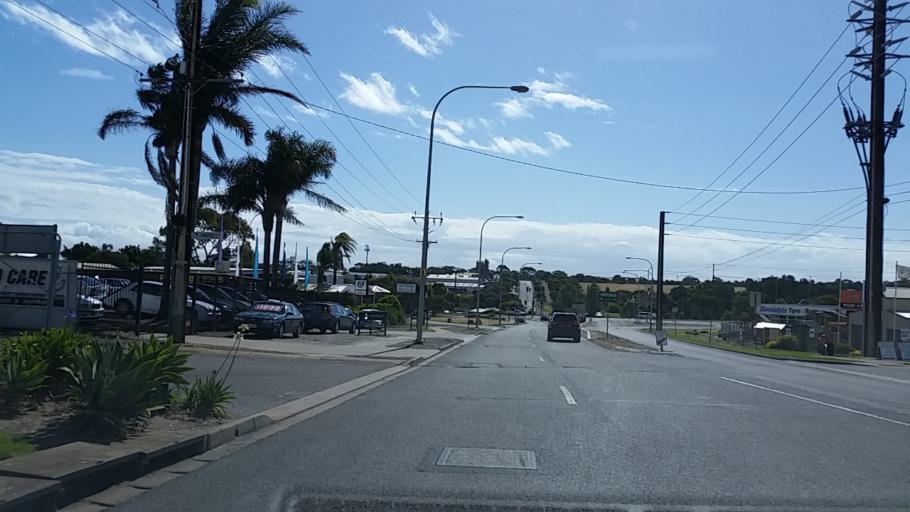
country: AU
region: South Australia
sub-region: Onkaparinga
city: Morphett Vale
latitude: -35.1173
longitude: 138.4927
